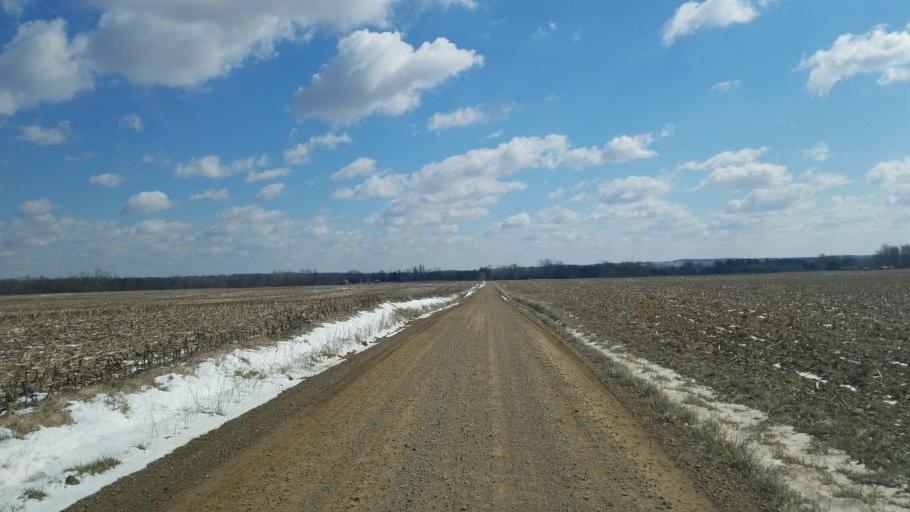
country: US
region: Ohio
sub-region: Licking County
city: Utica
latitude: 40.3026
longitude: -82.5013
